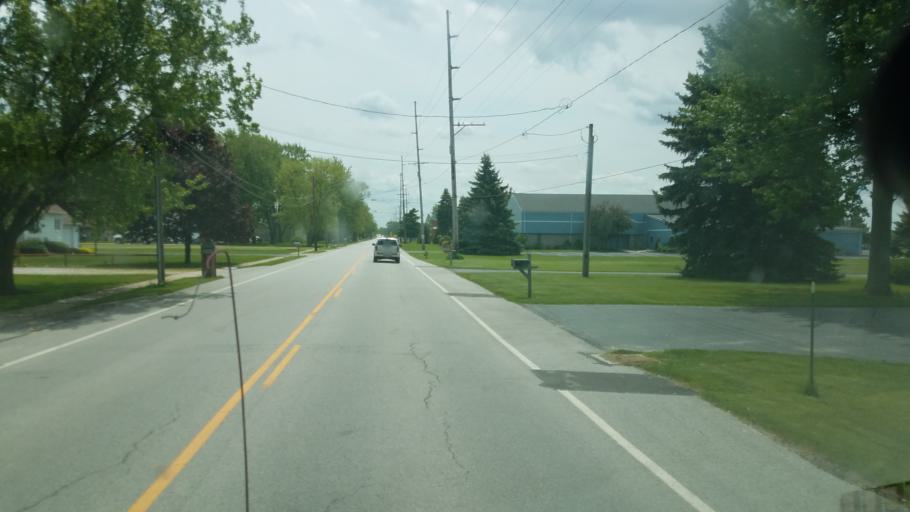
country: US
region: Ohio
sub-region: Sandusky County
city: Stony Prairie
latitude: 41.3588
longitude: -83.1463
